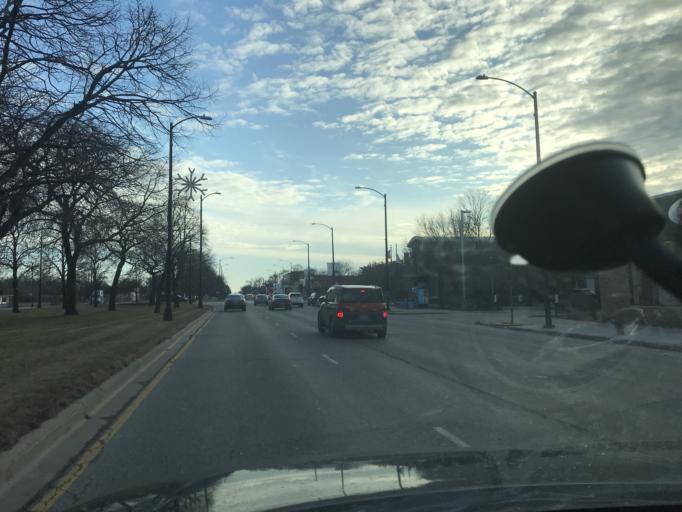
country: US
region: Illinois
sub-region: Cook County
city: Dolton
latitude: 41.7471
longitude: -87.5858
